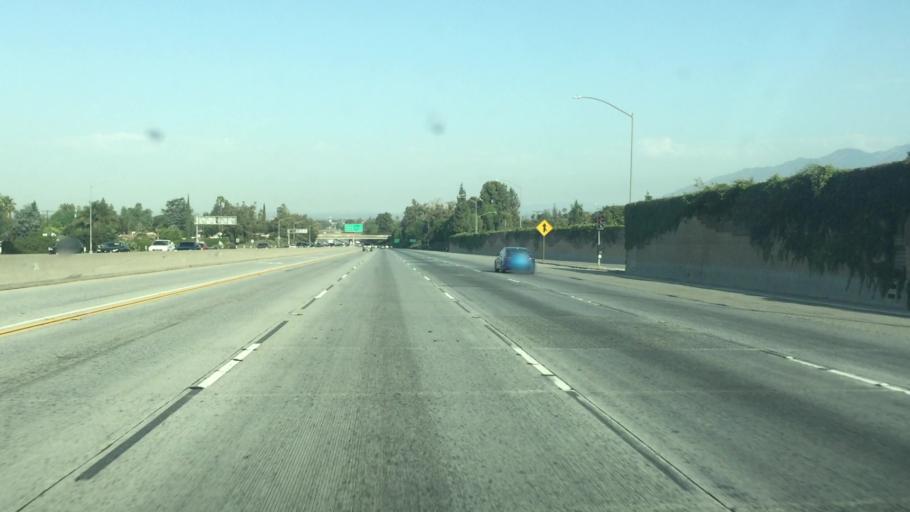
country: US
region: California
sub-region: Los Angeles County
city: Glendora
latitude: 34.1208
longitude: -117.8740
